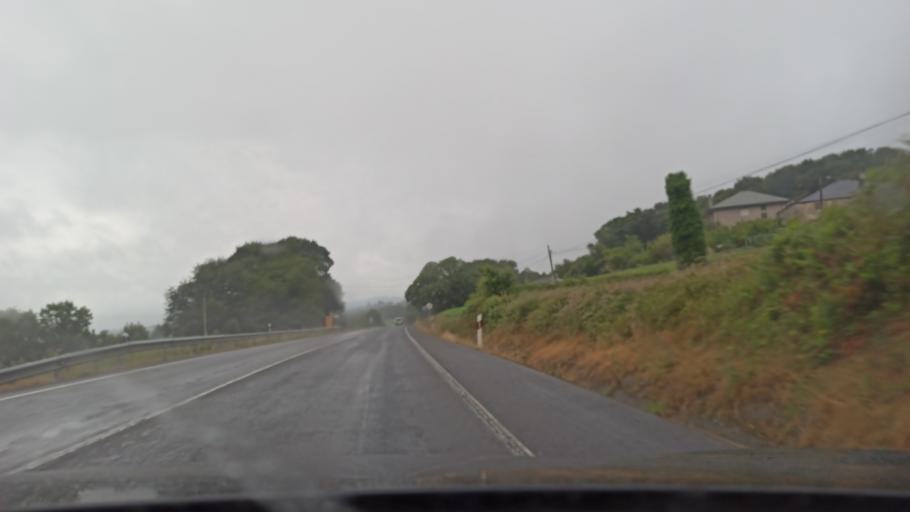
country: ES
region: Galicia
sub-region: Provincia de Lugo
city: Guntin
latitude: 42.9216
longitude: -7.6503
